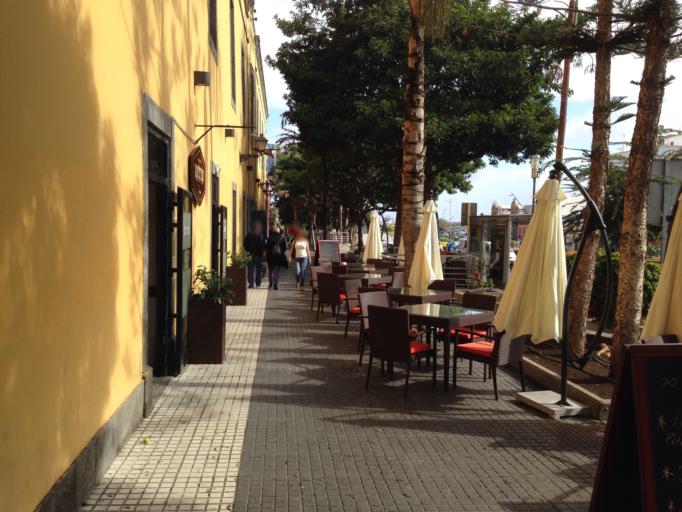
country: ES
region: Canary Islands
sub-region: Provincia de Las Palmas
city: Las Palmas de Gran Canaria
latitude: 28.1024
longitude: -15.4153
